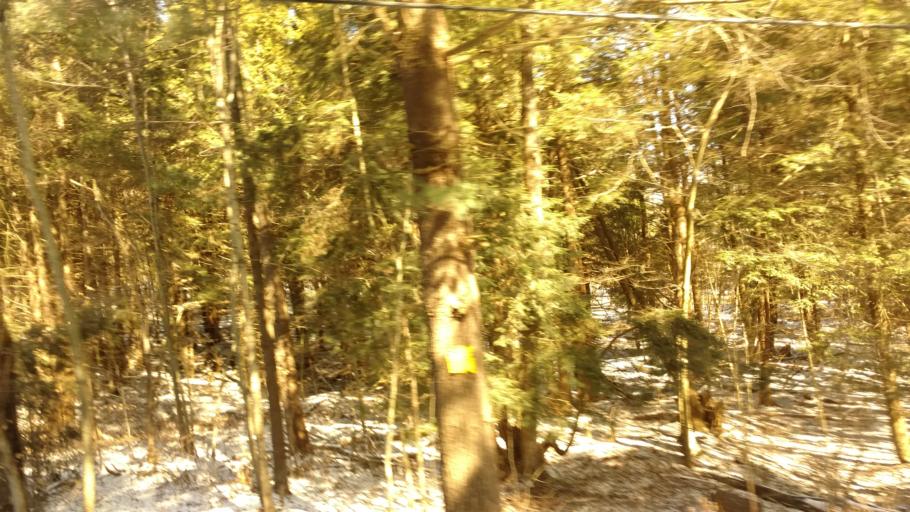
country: US
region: New York
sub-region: Allegany County
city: Wellsville
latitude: 42.0724
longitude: -77.9386
